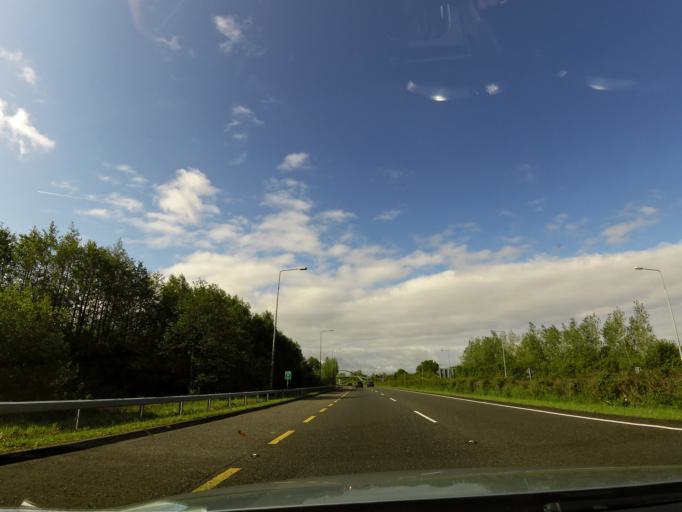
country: IE
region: Munster
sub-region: An Clar
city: Shannon
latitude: 52.7129
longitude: -8.8855
